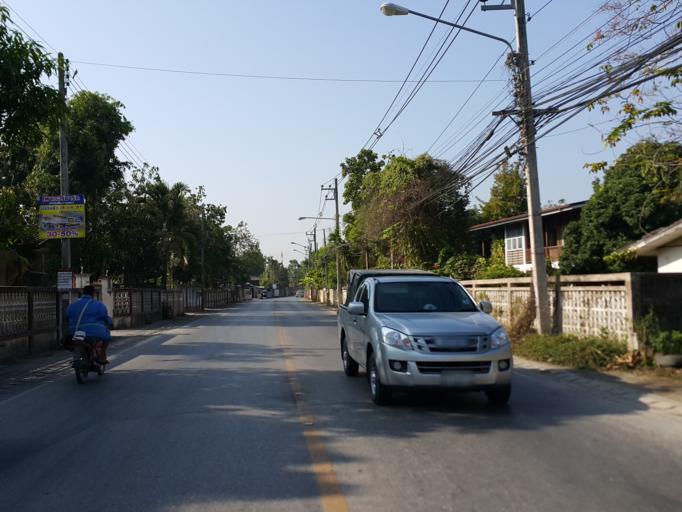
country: TH
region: Chiang Mai
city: San Kamphaeng
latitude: 18.7780
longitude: 99.0906
